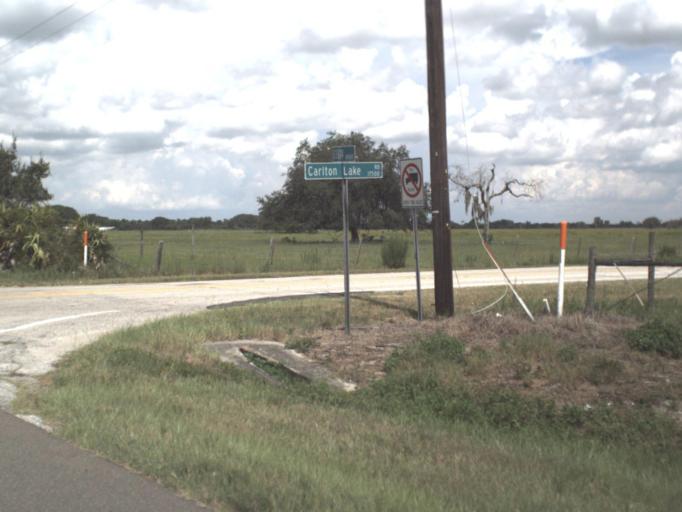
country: US
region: Florida
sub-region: Hillsborough County
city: Wimauma
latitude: 27.7050
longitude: -82.2446
